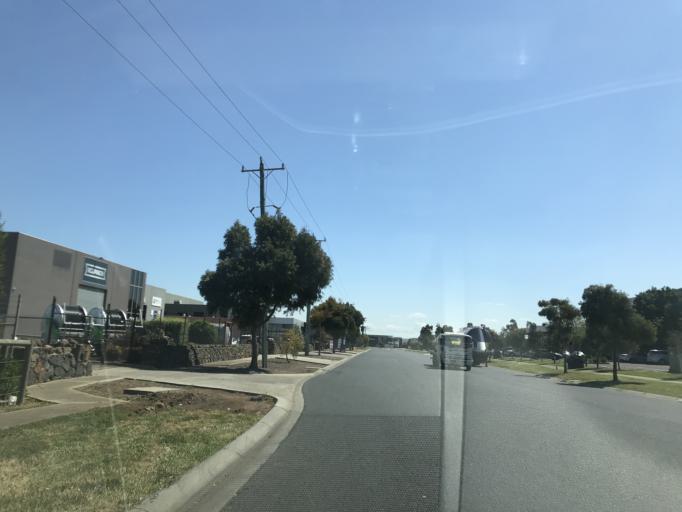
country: AU
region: Victoria
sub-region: Wyndham
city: Truganina
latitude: -37.8228
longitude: 144.7754
